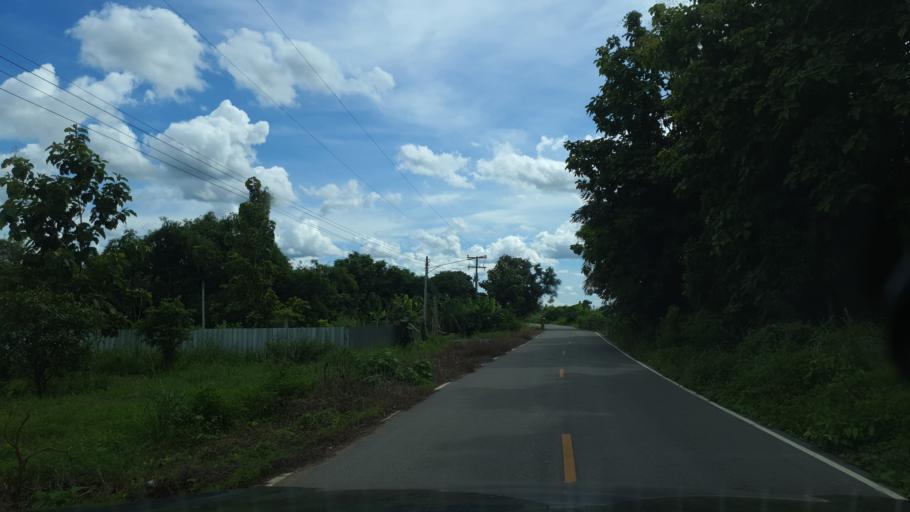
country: TH
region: Sukhothai
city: Thung Saliam
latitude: 17.3466
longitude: 99.6402
